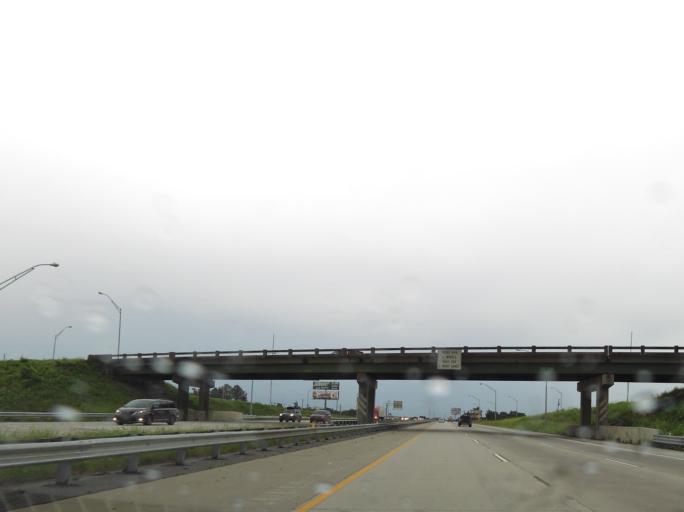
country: US
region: Georgia
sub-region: Dooly County
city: Unadilla
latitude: 32.2606
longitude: -83.7492
